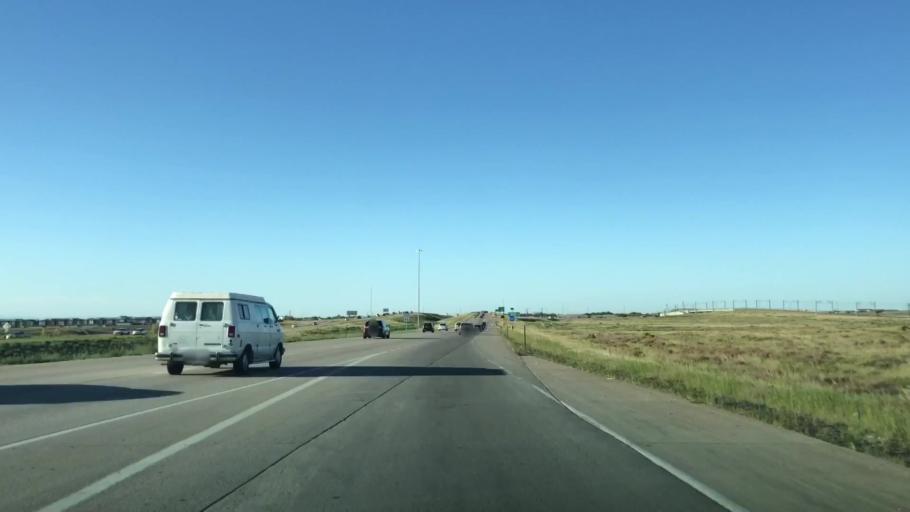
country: US
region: Colorado
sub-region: Adams County
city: Aurora
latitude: 39.7769
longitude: -104.7905
